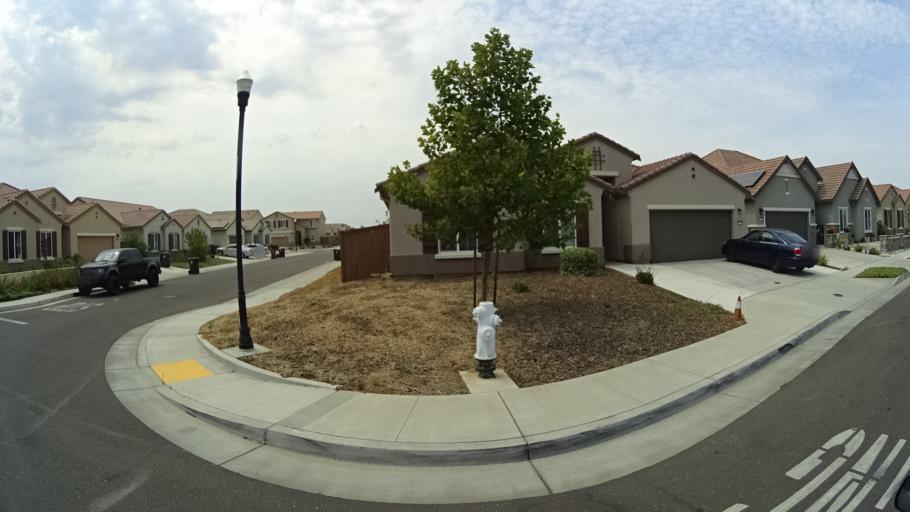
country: US
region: California
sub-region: Sacramento County
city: Laguna
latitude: 38.3920
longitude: -121.4099
